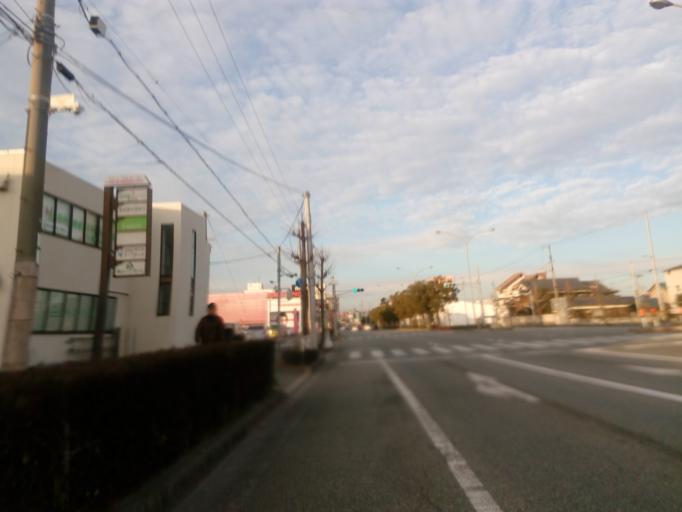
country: JP
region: Hyogo
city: Himeji
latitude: 34.8036
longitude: 134.6799
